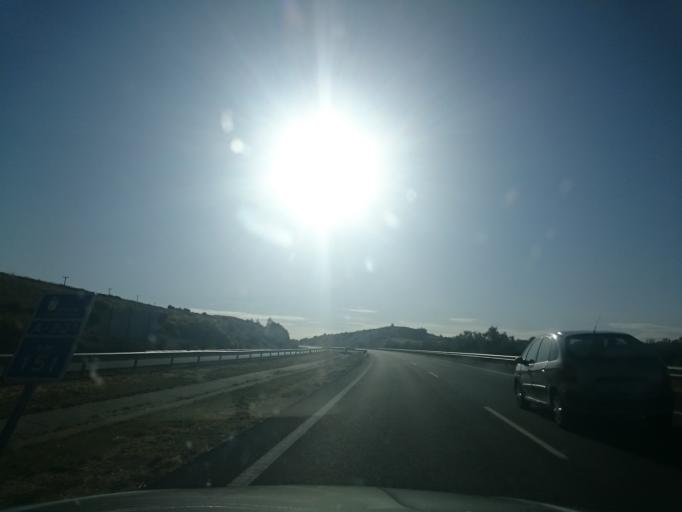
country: ES
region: Castille and Leon
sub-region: Provincia de Burgos
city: Rabe de las Calzadas
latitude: 42.3708
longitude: -3.8543
